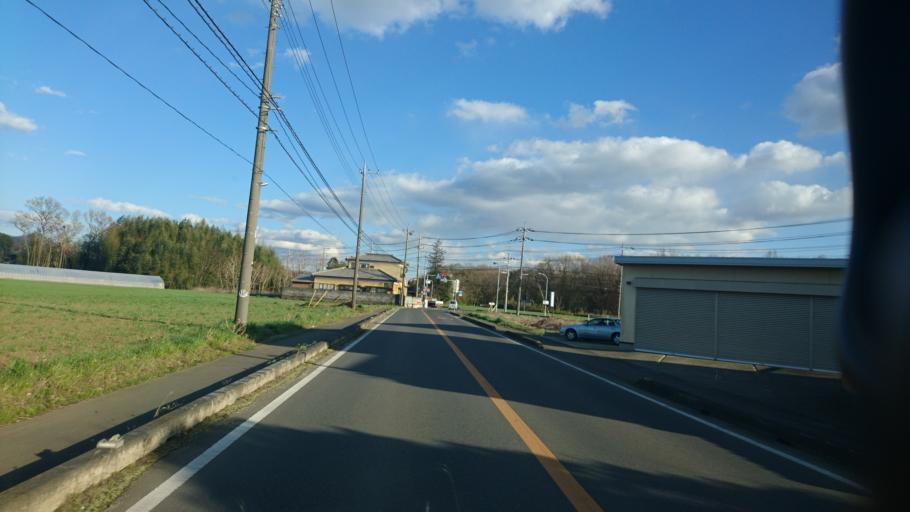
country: JP
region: Ibaraki
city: Shimodate
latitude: 36.2487
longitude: 139.9361
